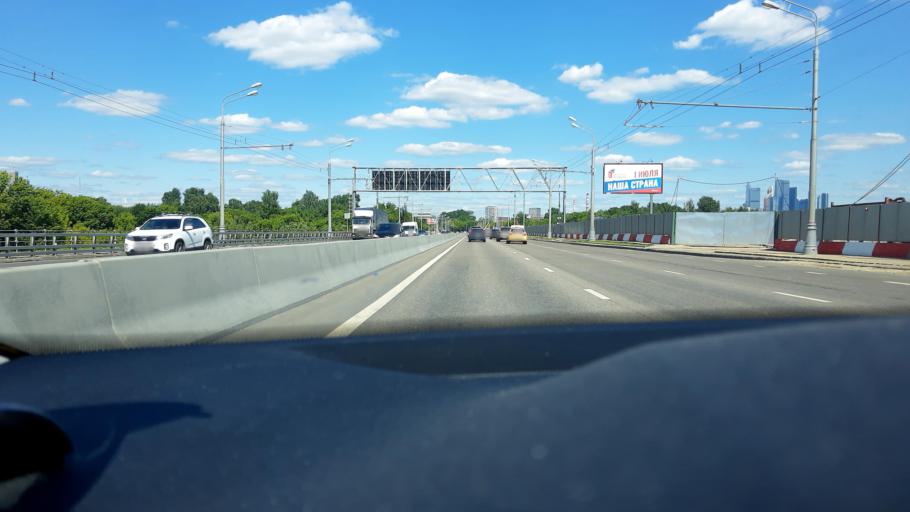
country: RU
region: Moskovskaya
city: Fili
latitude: 55.7484
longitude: 37.4459
